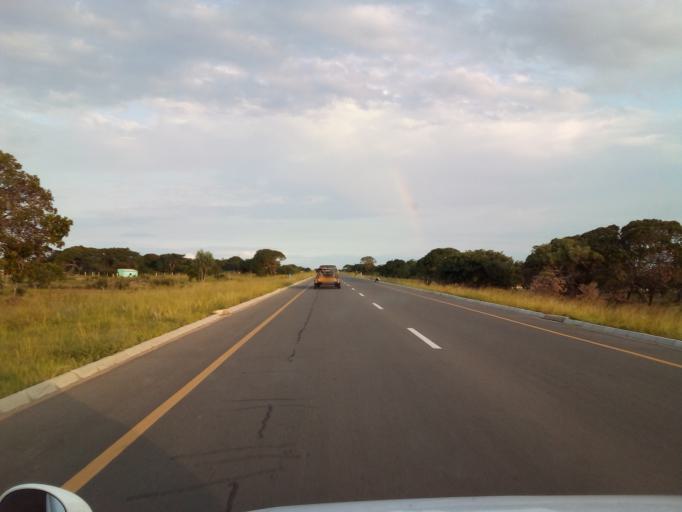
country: MZ
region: Maputo City
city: Maputo
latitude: -26.0598
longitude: 32.5919
